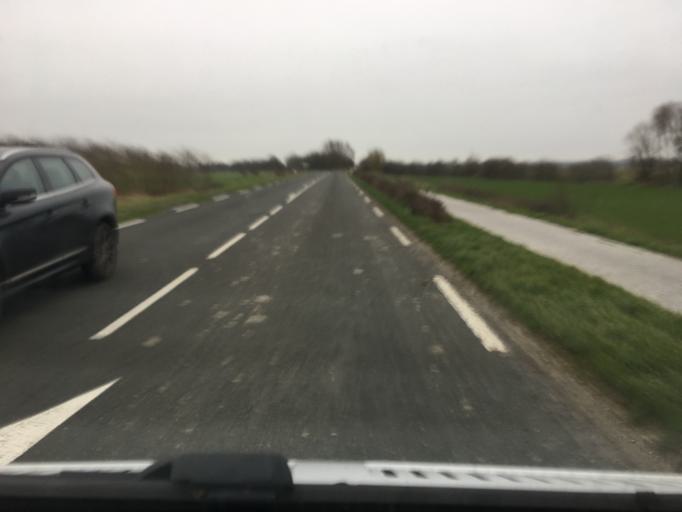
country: FR
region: Picardie
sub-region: Departement de la Somme
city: Pende
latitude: 50.1941
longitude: 1.5589
